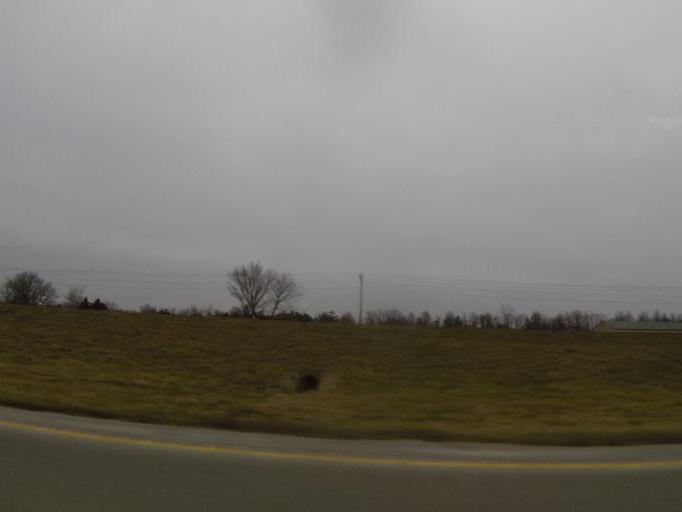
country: US
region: Missouri
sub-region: Ralls County
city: New London
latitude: 39.6519
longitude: -91.4197
